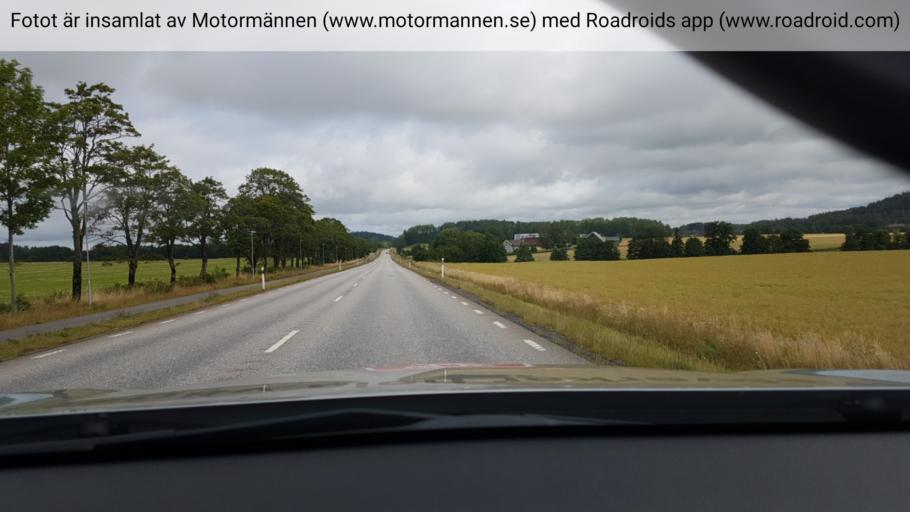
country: SE
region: Vaestra Goetaland
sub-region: Alingsas Kommun
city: Sollebrunn
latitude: 58.0940
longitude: 12.5016
